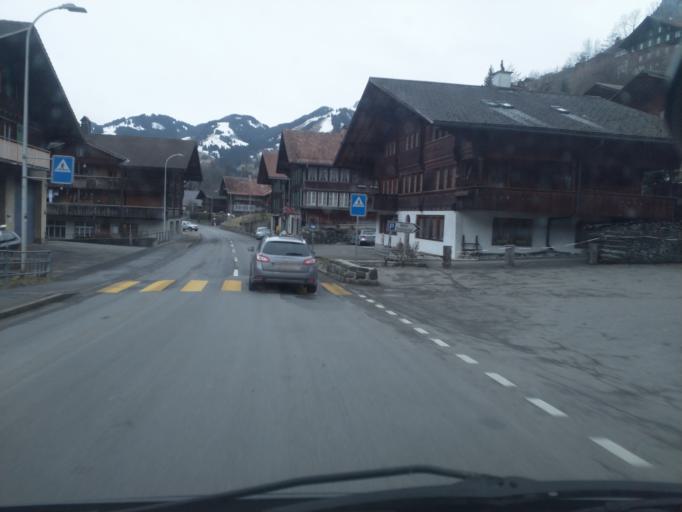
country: CH
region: Bern
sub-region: Obersimmental-Saanen District
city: Boltigen
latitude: 46.6289
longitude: 7.3901
